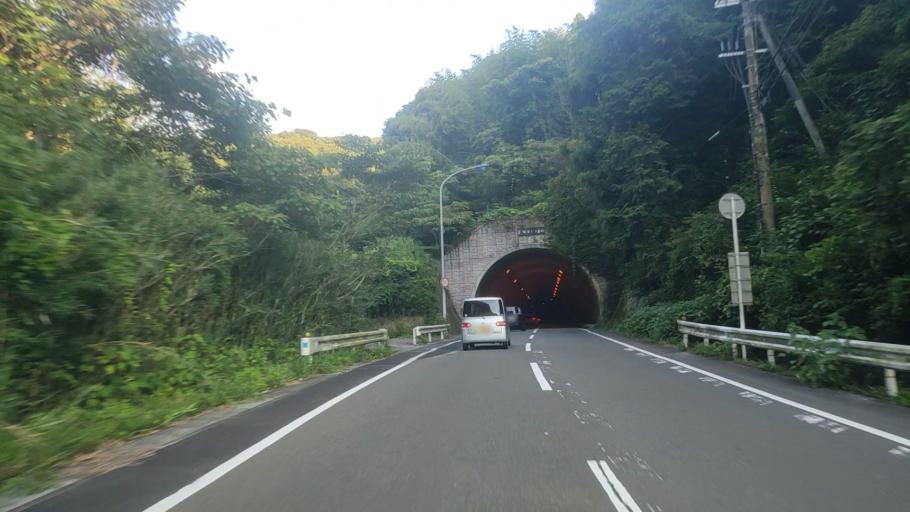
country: JP
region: Wakayama
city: Tanabe
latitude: 33.7310
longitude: 135.4344
